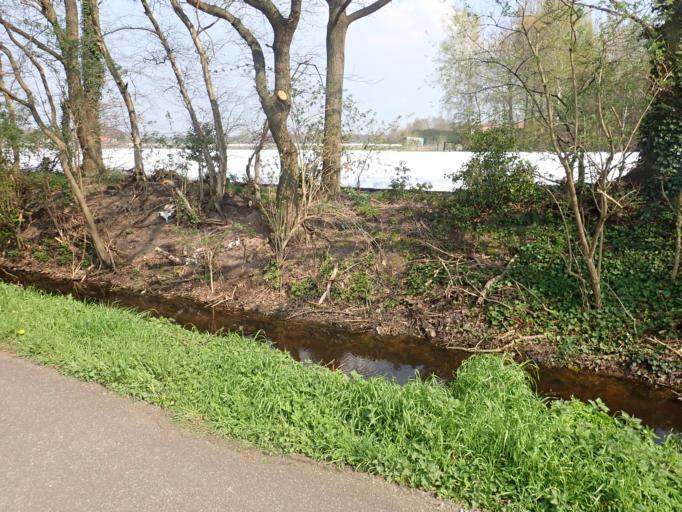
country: BE
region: Flanders
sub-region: Provincie Antwerpen
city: Essen
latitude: 51.4706
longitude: 4.5010
